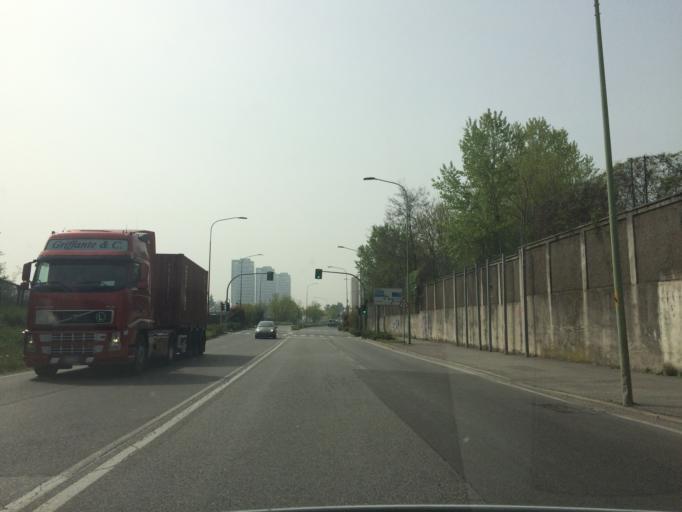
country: IT
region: Lombardy
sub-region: Provincia di Brescia
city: Brescia
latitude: 45.5289
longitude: 10.1992
